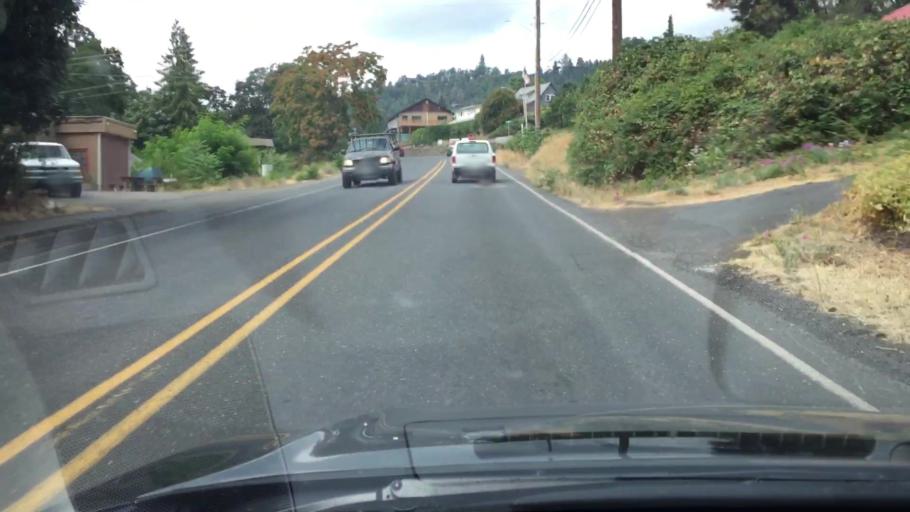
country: US
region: Washington
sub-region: Klickitat County
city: White Salmon
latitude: 45.7261
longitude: -121.4805
